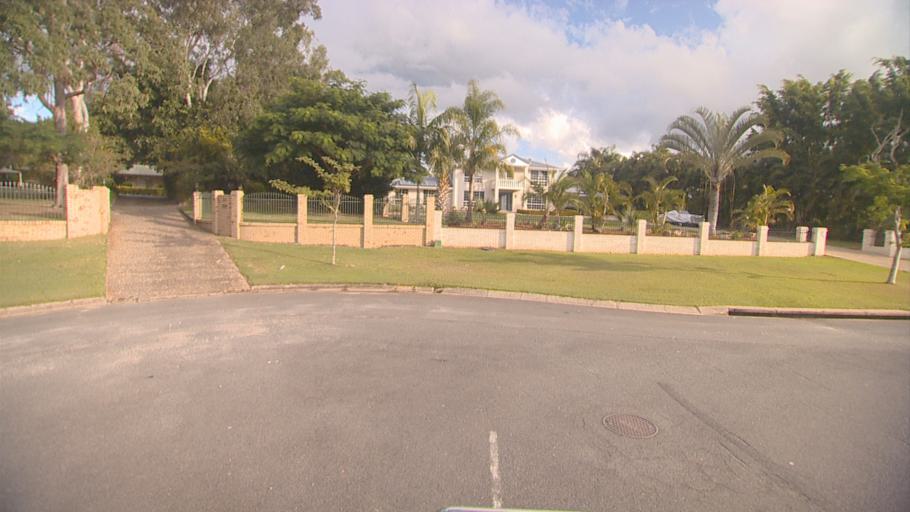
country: AU
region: Queensland
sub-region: Logan
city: Park Ridge South
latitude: -27.7063
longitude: 153.0238
